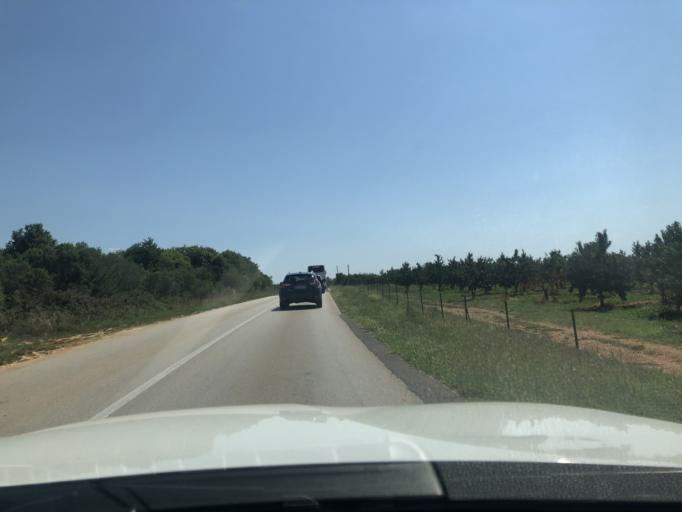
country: HR
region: Istarska
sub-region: Grad Rovinj
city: Rovinj
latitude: 45.0437
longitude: 13.7496
